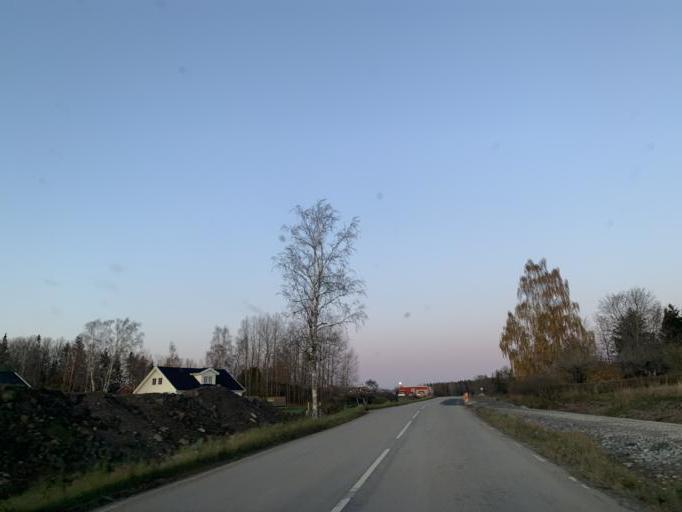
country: SE
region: OErebro
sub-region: Orebro Kommun
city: Hovsta
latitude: 59.3112
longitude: 15.3670
